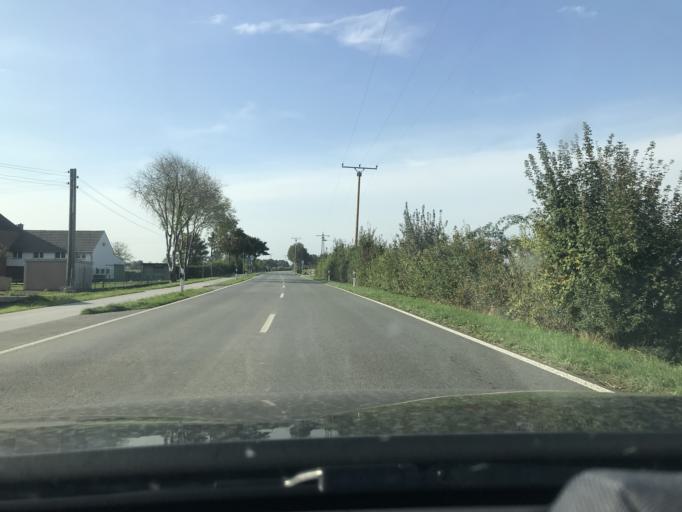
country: DE
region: North Rhine-Westphalia
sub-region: Regierungsbezirk Dusseldorf
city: Emmerich
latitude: 51.8031
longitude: 6.2286
